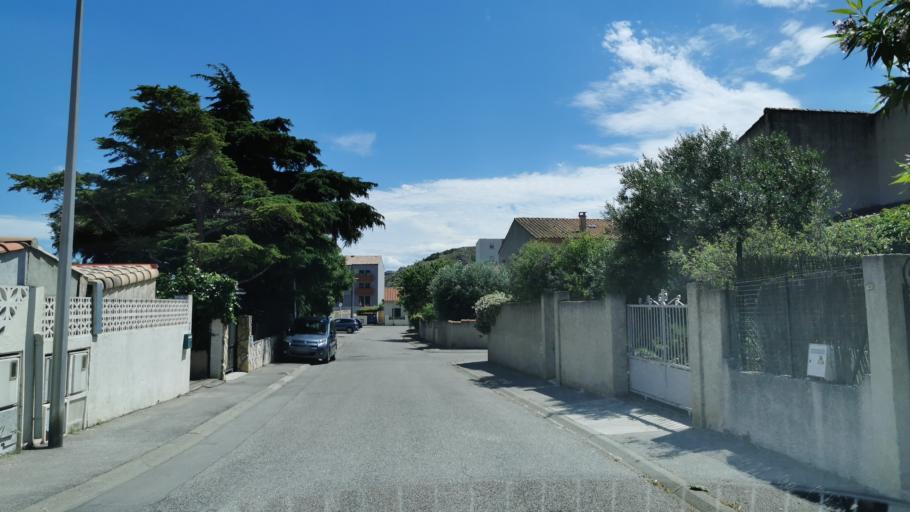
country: FR
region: Languedoc-Roussillon
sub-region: Departement de l'Aude
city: Narbonne
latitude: 43.1824
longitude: 2.9714
